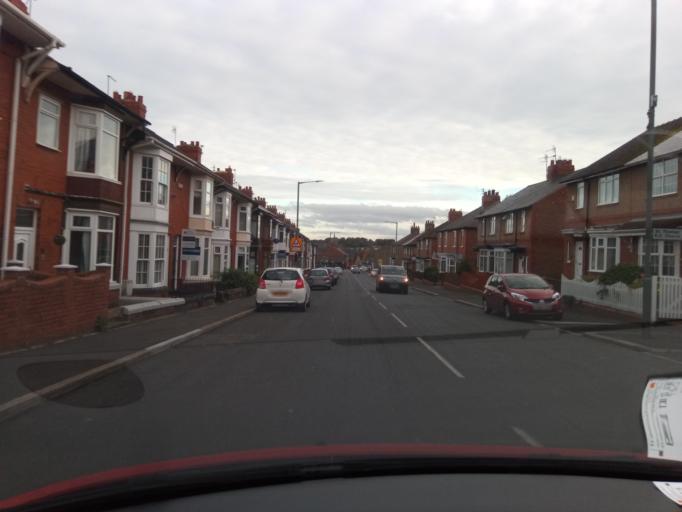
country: GB
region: England
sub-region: County Durham
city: Shildon
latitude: 54.6289
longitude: -1.6523
